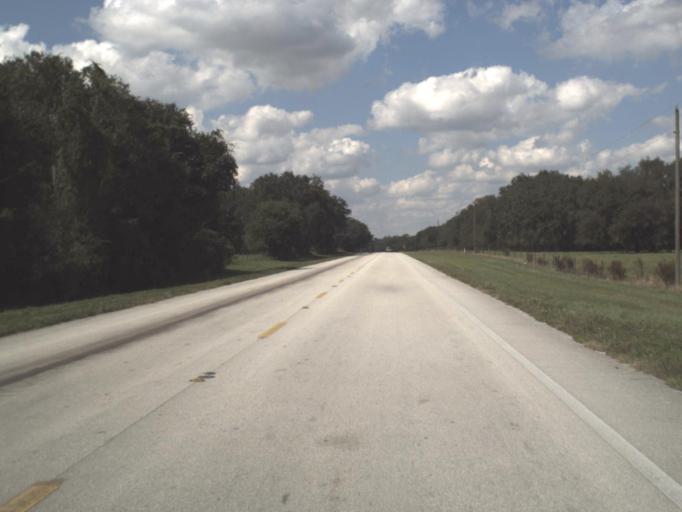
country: US
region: Florida
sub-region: Hardee County
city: Zolfo Springs
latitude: 27.4501
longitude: -81.6325
